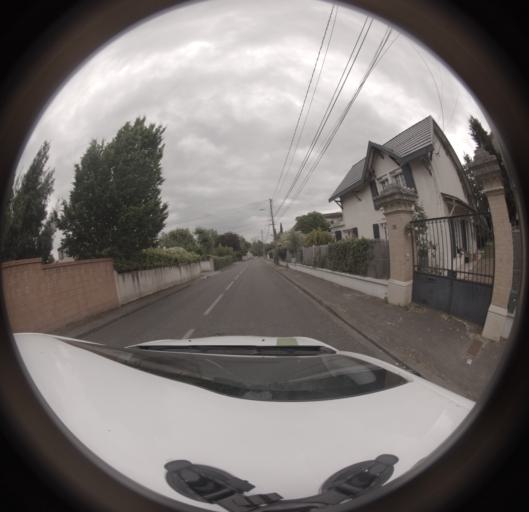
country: FR
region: Midi-Pyrenees
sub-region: Departement du Tarn-et-Garonne
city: Montauban
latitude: 44.0073
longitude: 1.3675
